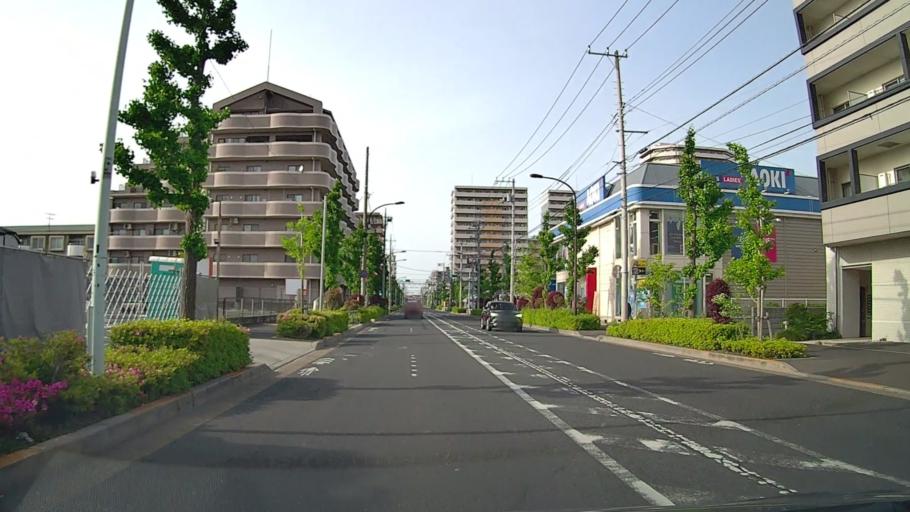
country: JP
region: Saitama
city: Soka
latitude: 35.7839
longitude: 139.7858
